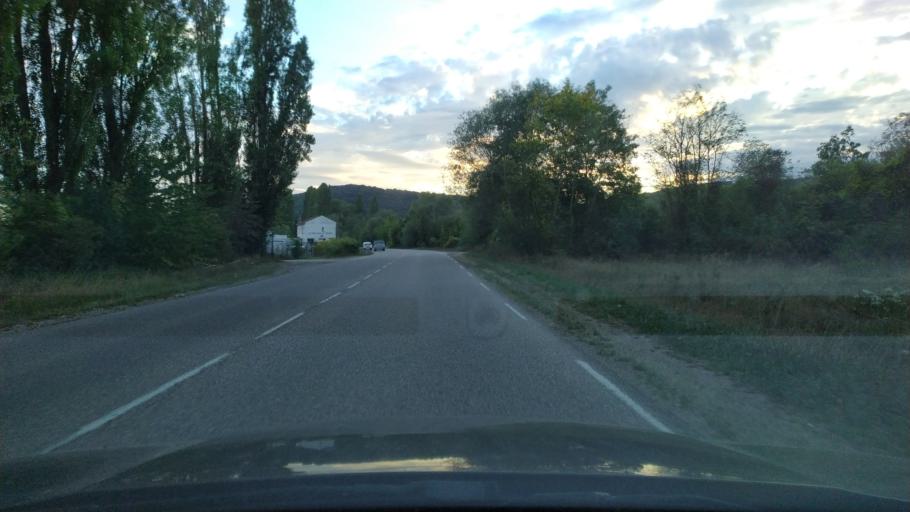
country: FR
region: Lorraine
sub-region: Departement de la Moselle
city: Moulins-les-Metz
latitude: 49.0975
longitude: 6.1022
